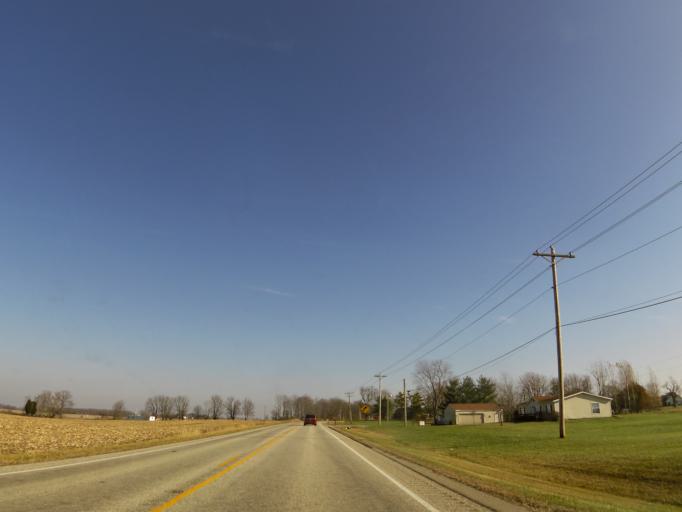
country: US
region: Indiana
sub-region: Rush County
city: Rushville
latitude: 39.5953
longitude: -85.5124
